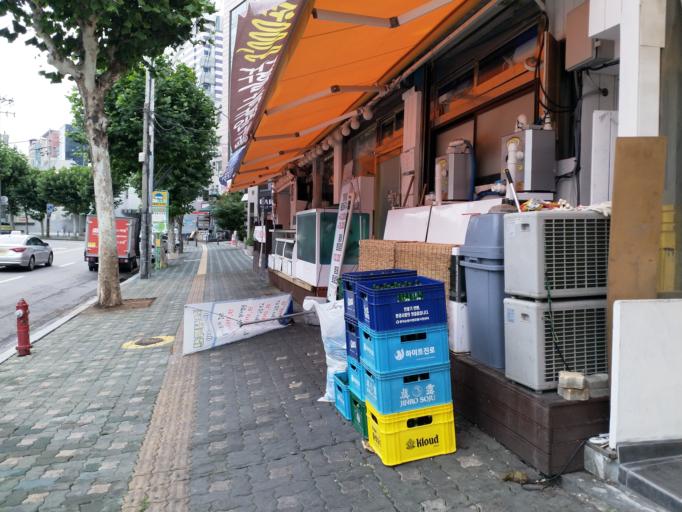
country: KR
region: Seoul
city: Seoul
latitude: 37.5561
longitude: 126.9208
